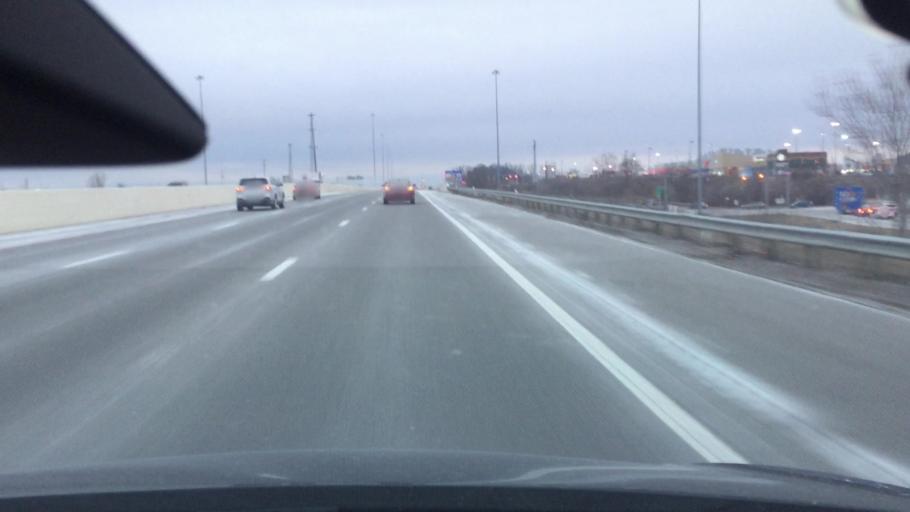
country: US
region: Ohio
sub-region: Stark County
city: North Canton
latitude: 40.8815
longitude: -81.4317
